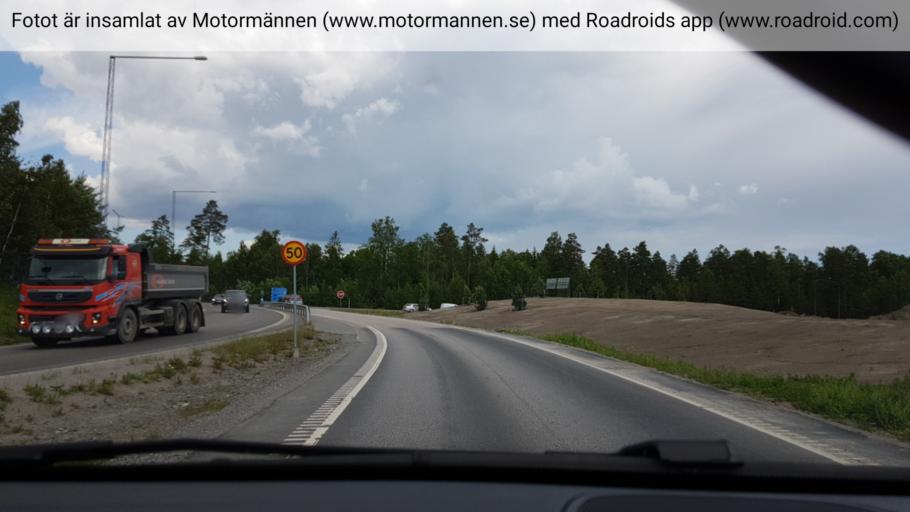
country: SE
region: Stockholm
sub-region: Haninge Kommun
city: Haninge
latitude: 59.1534
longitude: 18.1577
